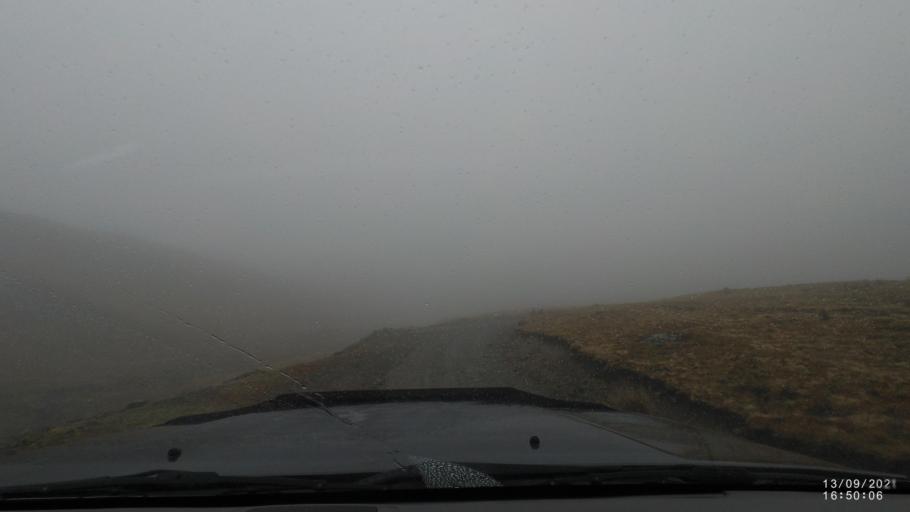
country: BO
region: Cochabamba
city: Colomi
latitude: -17.3035
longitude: -65.7067
